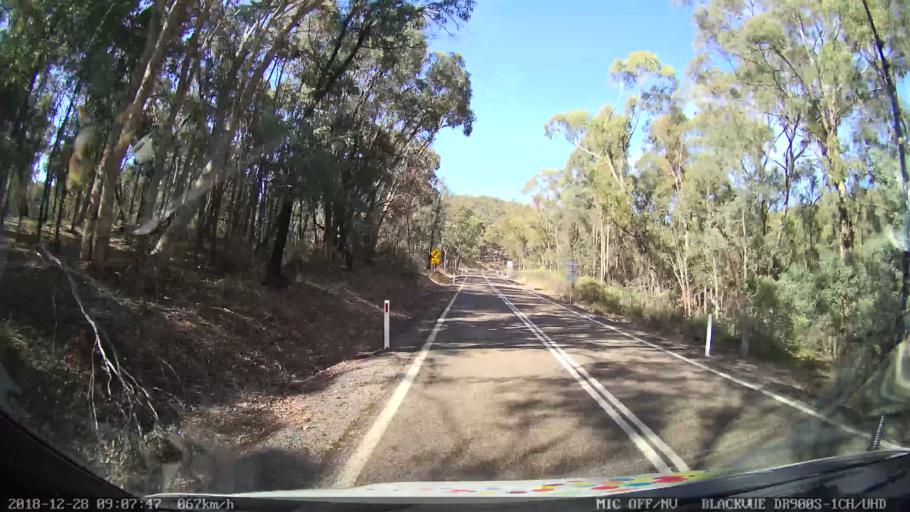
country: AU
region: New South Wales
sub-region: Upper Lachlan Shire
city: Crookwell
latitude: -34.2103
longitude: 149.3445
